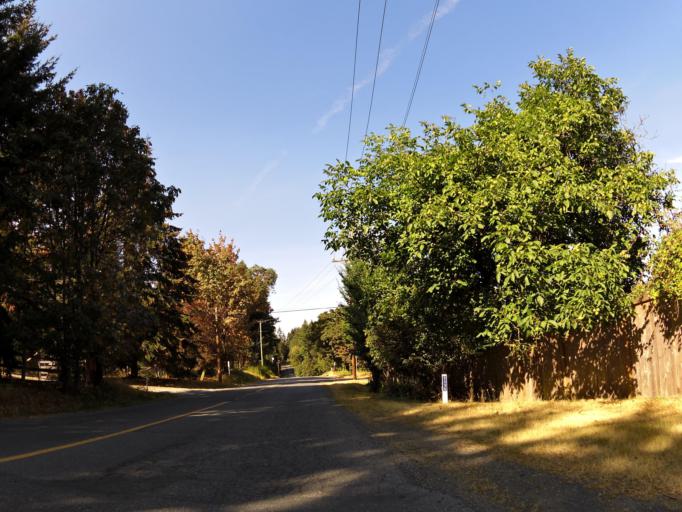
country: CA
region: British Columbia
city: North Saanich
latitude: 48.6788
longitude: -123.5506
